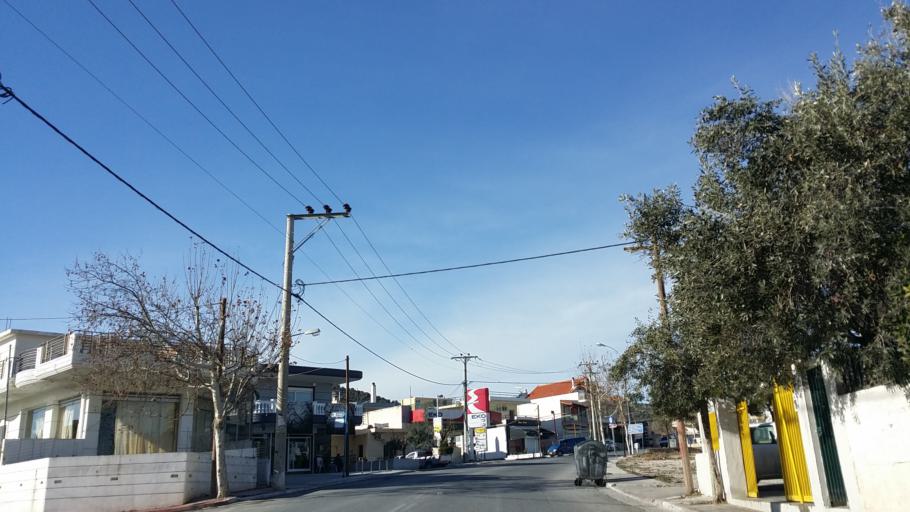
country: GR
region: Attica
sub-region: Nomarchia Dytikis Attikis
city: Ano Liosia
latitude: 38.0905
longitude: 23.6898
